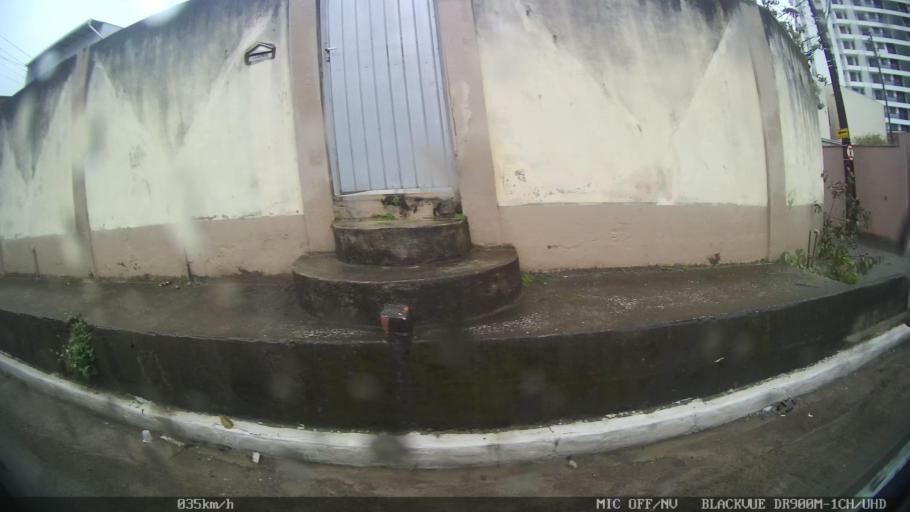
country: BR
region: Santa Catarina
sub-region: Itajai
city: Itajai
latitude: -26.9285
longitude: -48.6847
